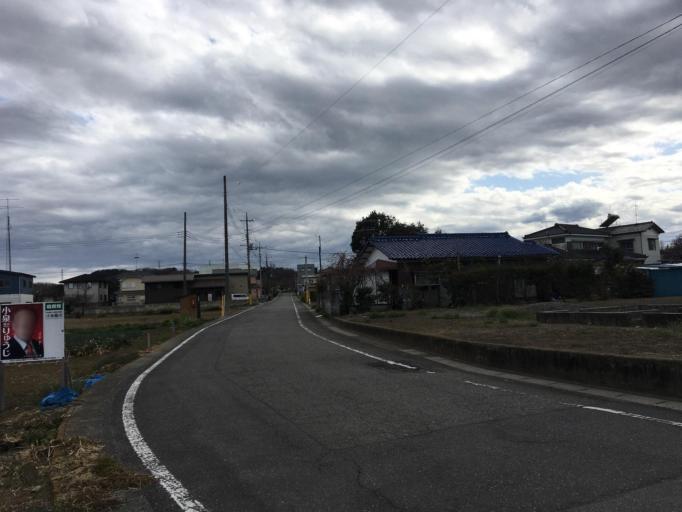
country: JP
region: Saitama
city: Ogawa
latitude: 36.1112
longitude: 139.2546
